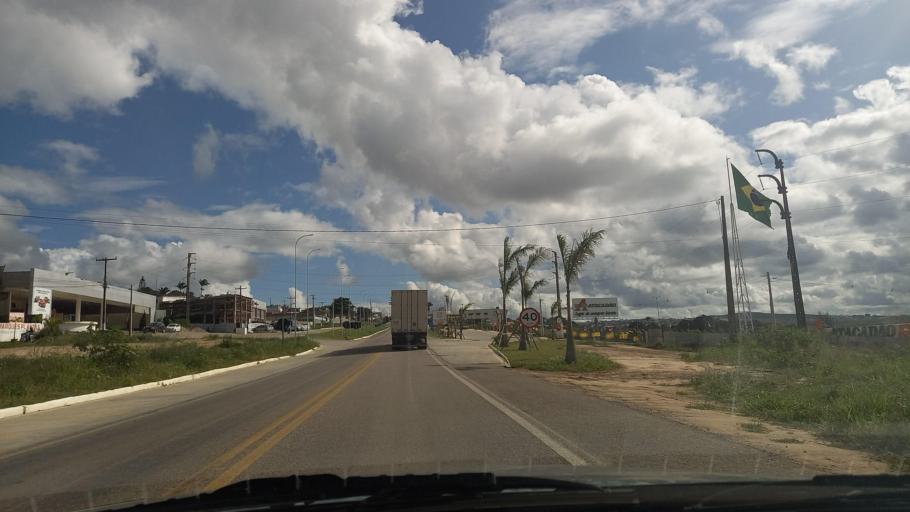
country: BR
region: Pernambuco
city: Garanhuns
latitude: -8.8714
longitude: -36.4658
